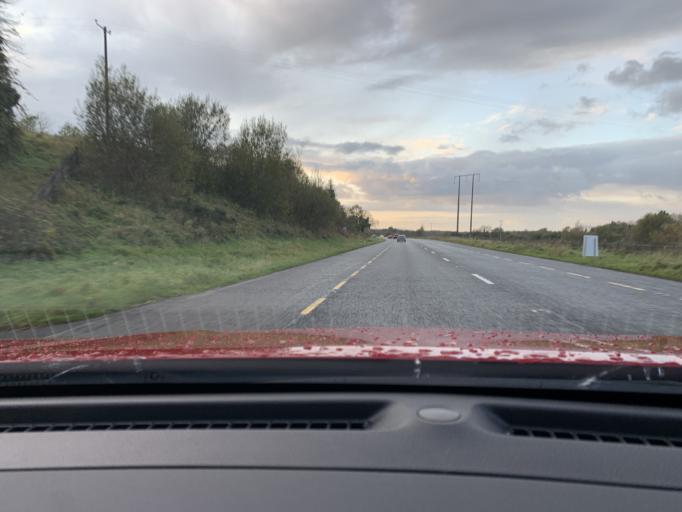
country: IE
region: Connaught
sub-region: County Leitrim
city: Carrick-on-Shannon
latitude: 53.9467
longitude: -8.1210
